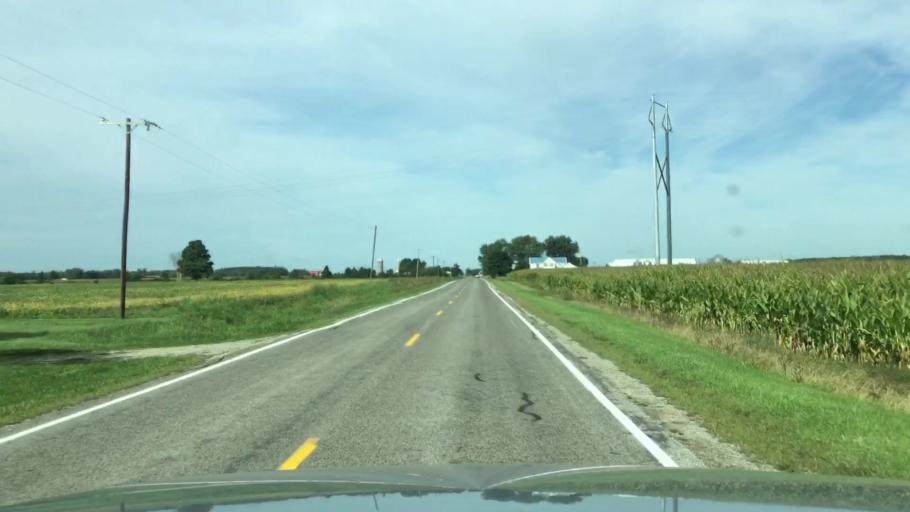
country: US
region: Michigan
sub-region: Genesee County
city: Montrose
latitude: 43.1469
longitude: -83.9707
